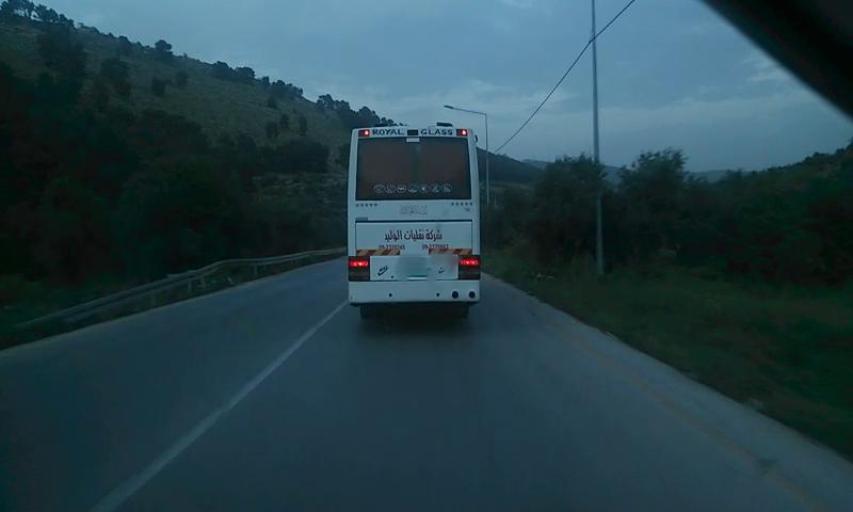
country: PS
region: West Bank
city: Kafr al Labad
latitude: 32.3175
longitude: 35.0906
